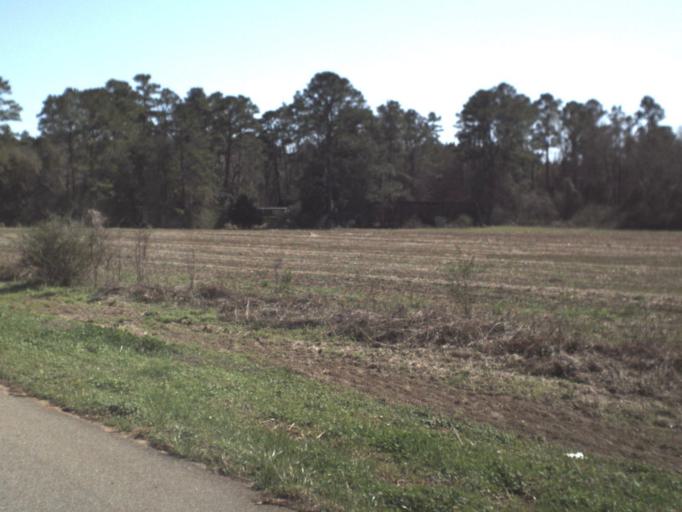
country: US
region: Florida
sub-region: Jackson County
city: Marianna
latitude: 30.8180
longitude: -85.3157
